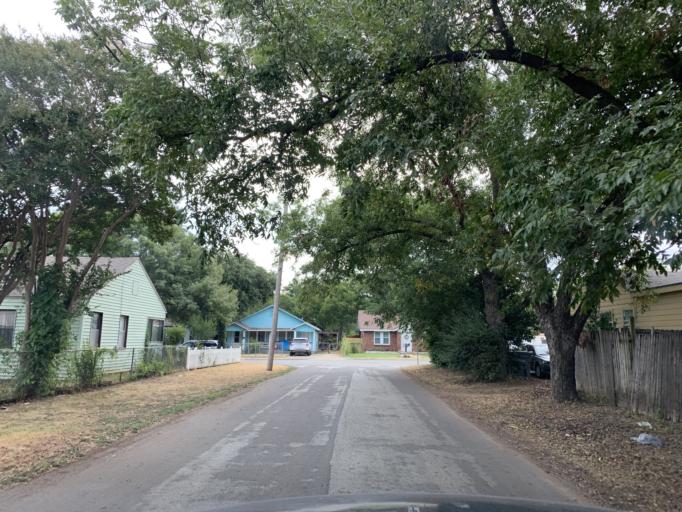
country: US
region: Texas
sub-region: Dallas County
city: Cockrell Hill
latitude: 32.7535
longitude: -96.8706
